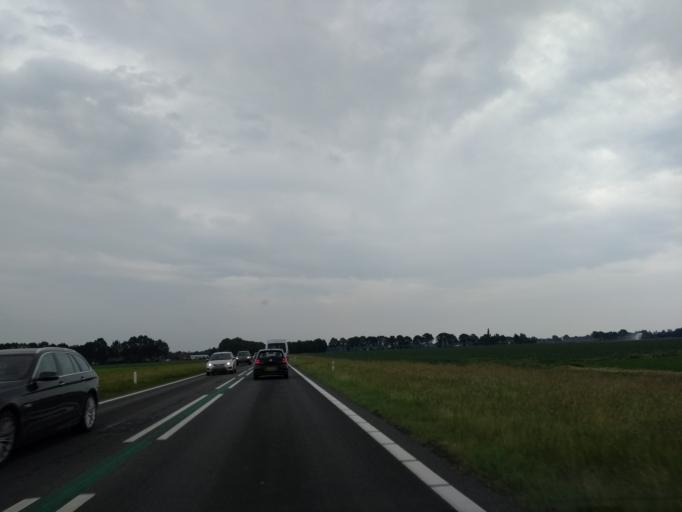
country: NL
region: Overijssel
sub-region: Gemeente Twenterand
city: Westerhaar-Vriezenveensewijk
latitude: 52.4799
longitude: 6.6128
